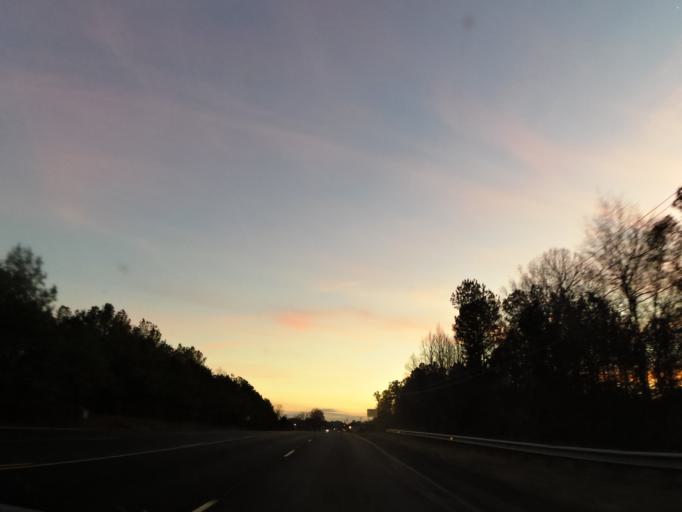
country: US
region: Georgia
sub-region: Whitfield County
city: Varnell
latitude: 34.9634
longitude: -84.9369
